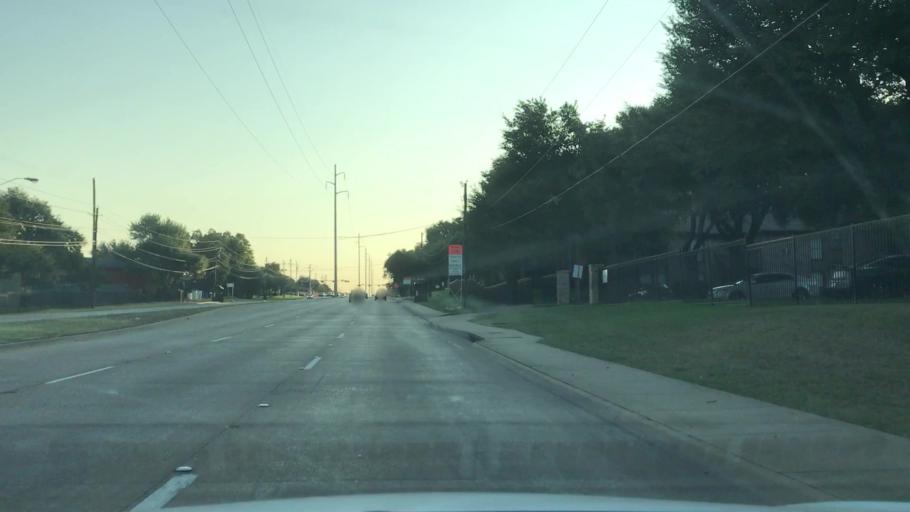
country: US
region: Texas
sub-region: Dallas County
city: Richardson
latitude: 32.8922
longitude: -96.7270
